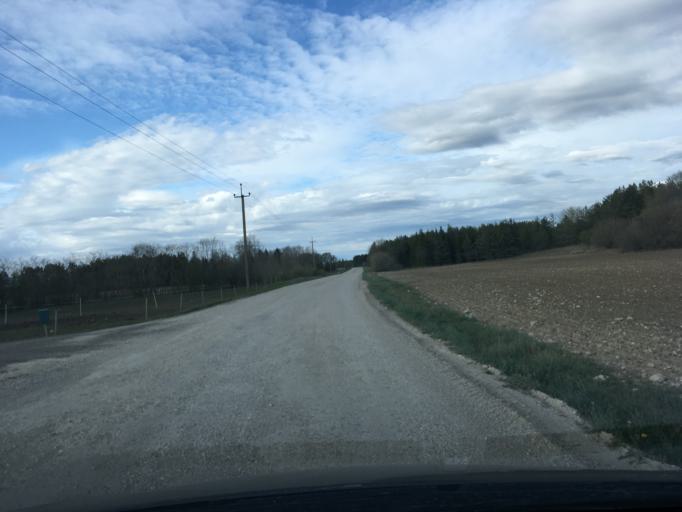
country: EE
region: Raplamaa
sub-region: Maerjamaa vald
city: Marjamaa
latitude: 58.9384
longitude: 24.3101
